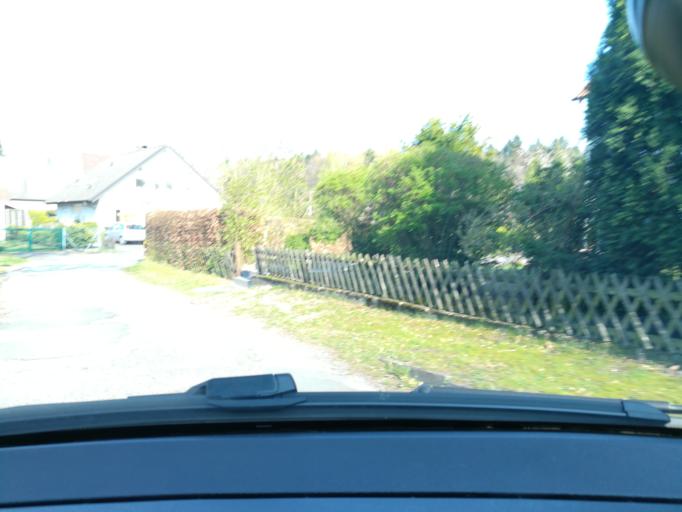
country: DE
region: North Rhine-Westphalia
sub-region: Regierungsbezirk Detmold
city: Oerlinghausen
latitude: 51.9290
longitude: 8.6056
